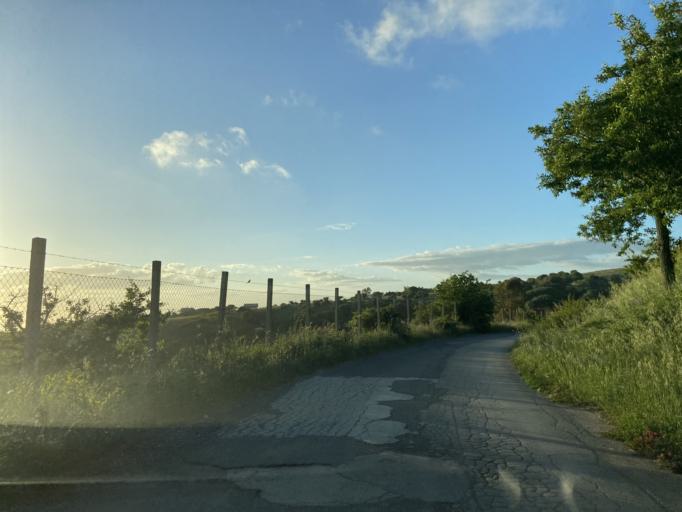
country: IT
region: Latium
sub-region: Citta metropolitana di Roma Capitale
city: Santa Marinella
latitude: 42.0820
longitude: 11.8493
